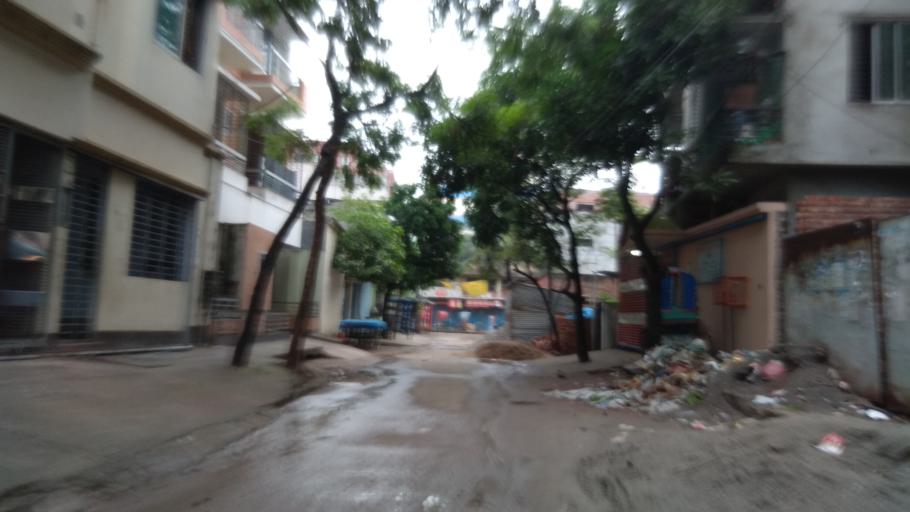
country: BD
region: Dhaka
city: Tungi
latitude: 23.8200
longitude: 90.3765
